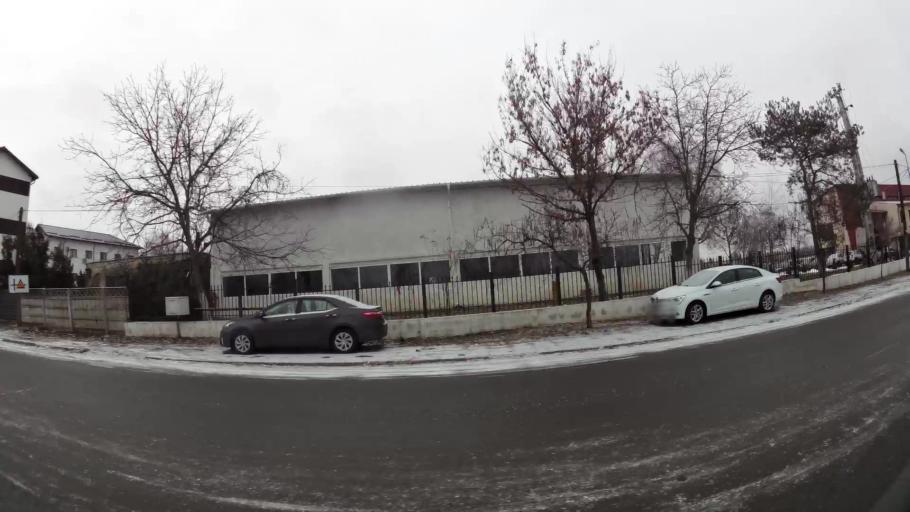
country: RO
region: Dambovita
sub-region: Municipiul Targoviste
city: Targoviste
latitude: 44.9312
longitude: 25.4753
